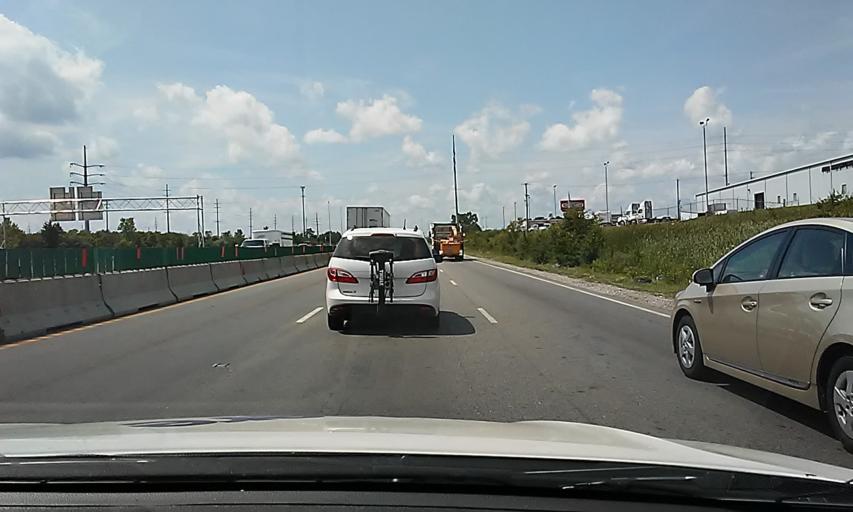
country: US
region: Ohio
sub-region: Franklin County
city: Lincoln Village
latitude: 39.9771
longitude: -83.1373
